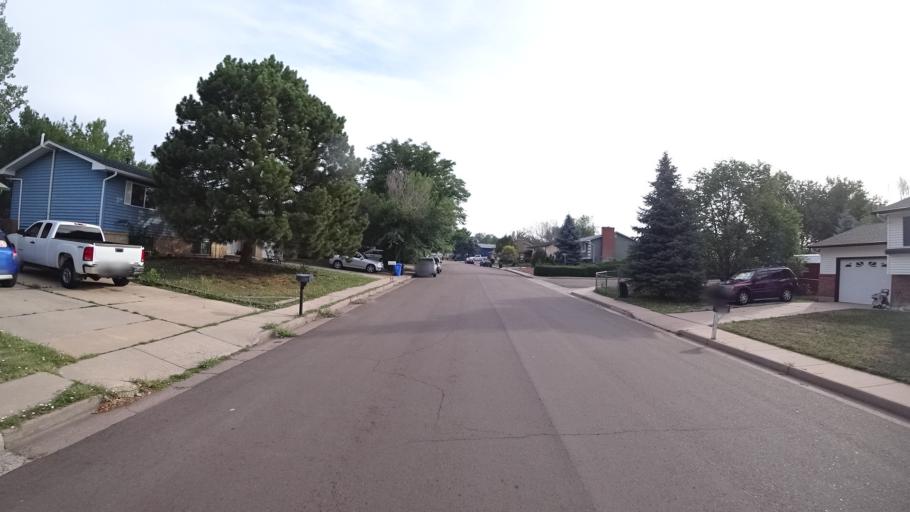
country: US
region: Colorado
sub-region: El Paso County
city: Security-Widefield
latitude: 38.7287
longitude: -104.6929
